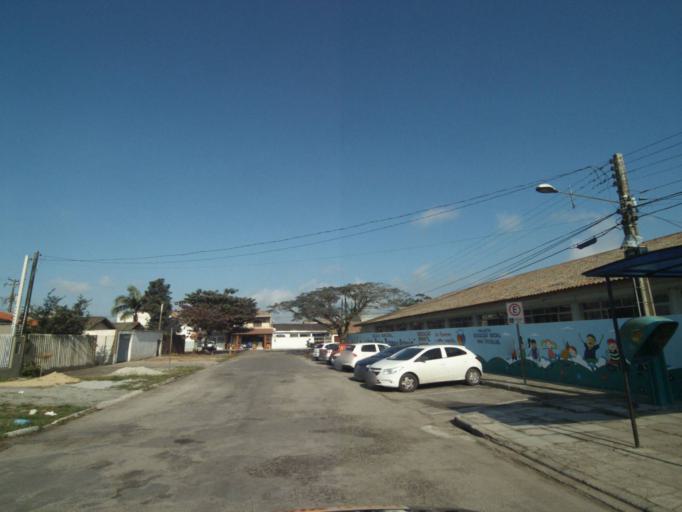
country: BR
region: Parana
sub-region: Paranagua
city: Paranagua
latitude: -25.5559
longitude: -48.5585
